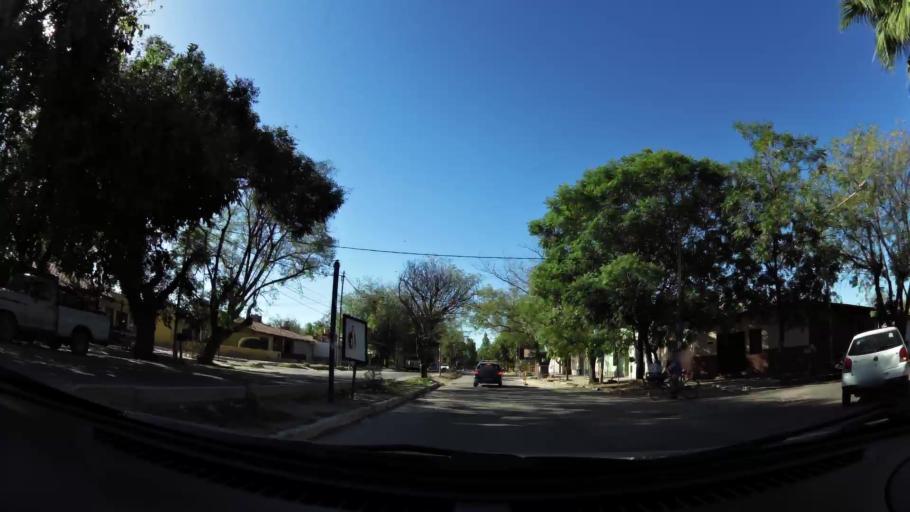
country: AR
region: Mendoza
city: Las Heras
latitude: -32.8562
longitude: -68.8215
